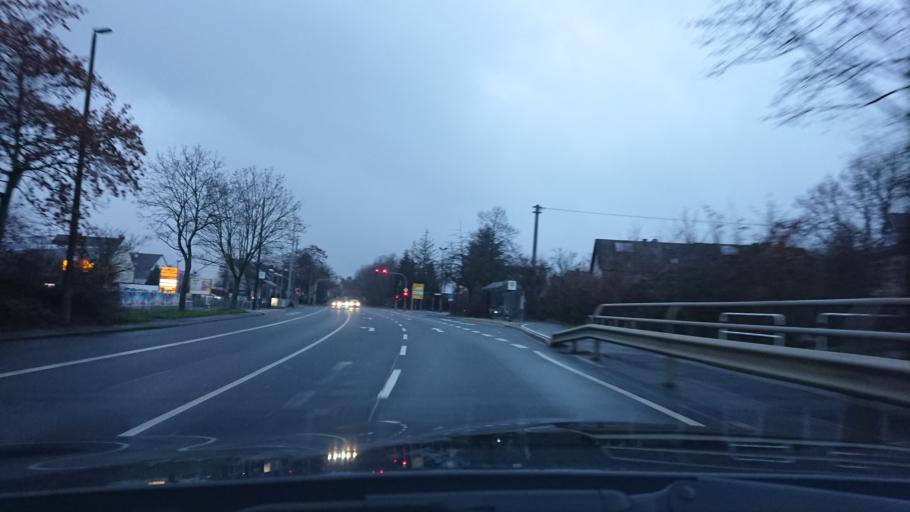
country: DE
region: North Rhine-Westphalia
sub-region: Regierungsbezirk Koln
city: Bonn
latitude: 50.7779
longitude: 7.0796
